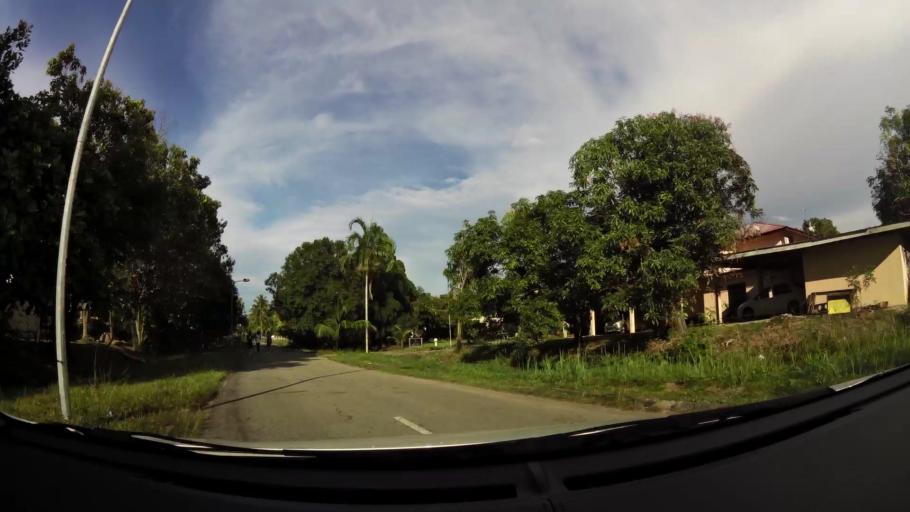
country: BN
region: Brunei and Muara
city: Bandar Seri Begawan
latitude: 4.9877
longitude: 114.9739
